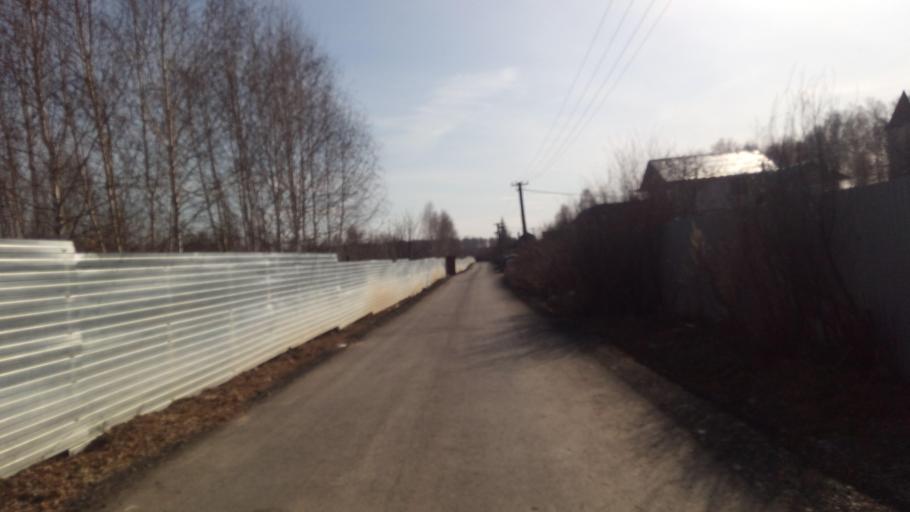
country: RU
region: Chelyabinsk
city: Sargazy
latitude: 55.1230
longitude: 61.2445
